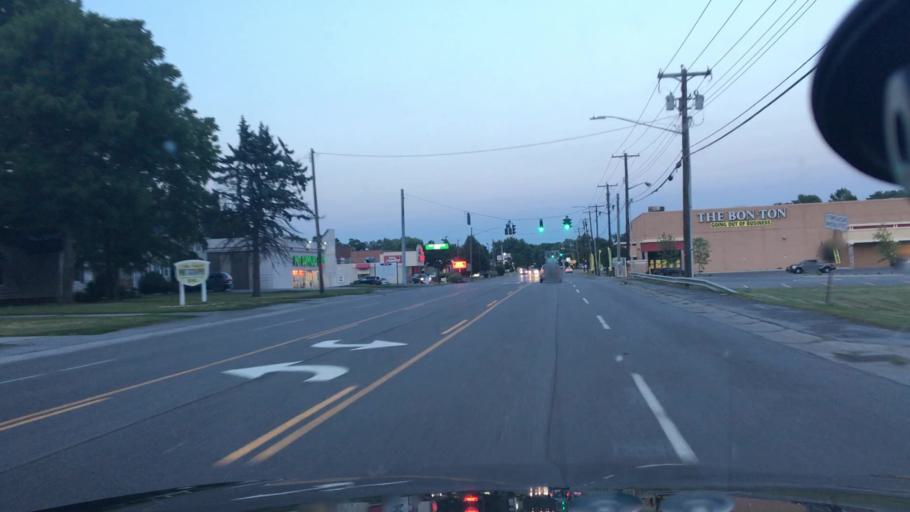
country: US
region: New York
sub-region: Erie County
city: West Seneca
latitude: 42.8300
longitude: -78.7568
